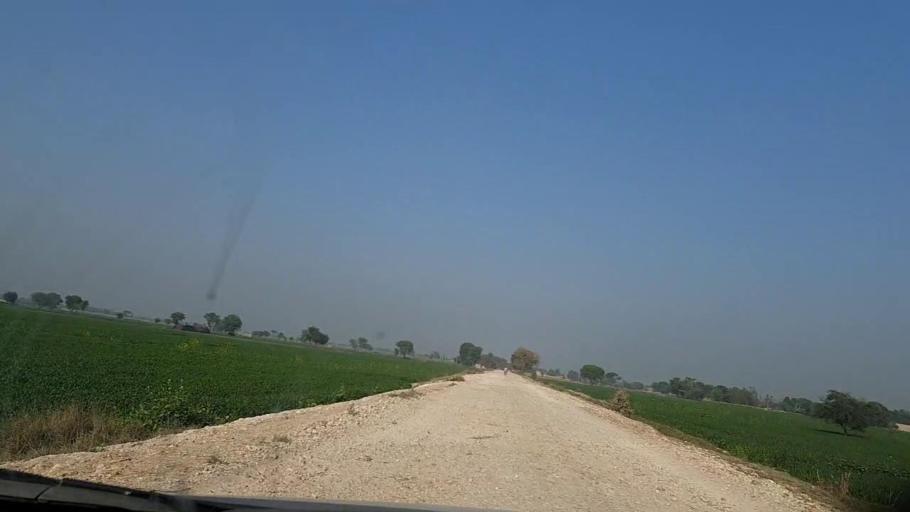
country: PK
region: Sindh
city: Moro
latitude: 26.7715
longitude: 67.9319
